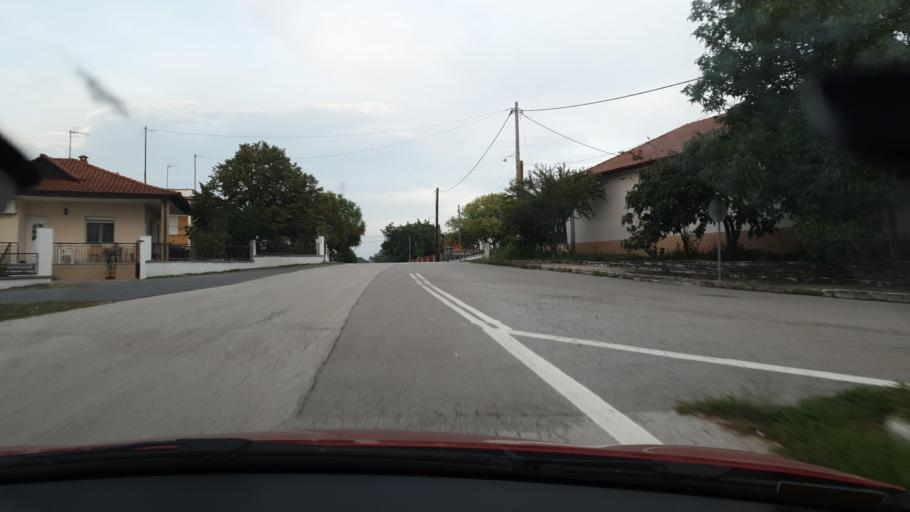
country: GR
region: Central Macedonia
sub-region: Nomos Kilkis
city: Kristoni
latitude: 40.9516
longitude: 22.8236
